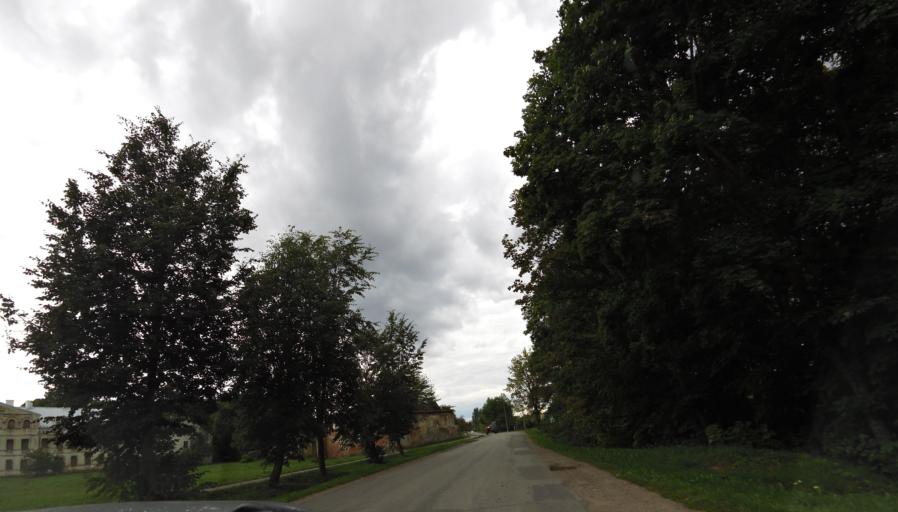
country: LT
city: Linkuva
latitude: 56.0319
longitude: 24.1657
